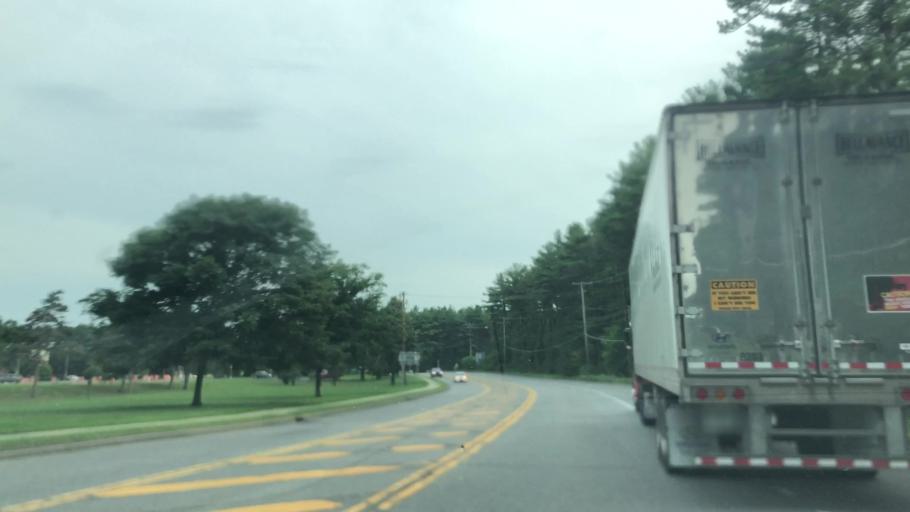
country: US
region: New York
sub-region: Warren County
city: Glens Falls North
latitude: 43.3613
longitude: -73.7014
